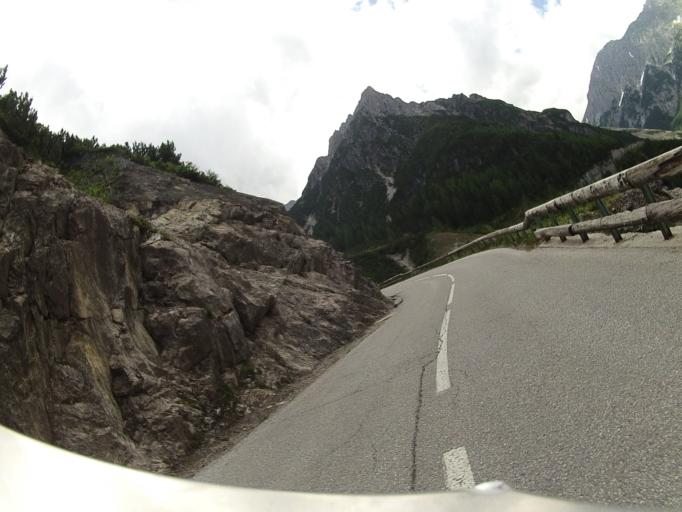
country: AT
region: Tyrol
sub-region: Politischer Bezirk Imst
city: Imst
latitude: 47.2811
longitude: 10.7122
